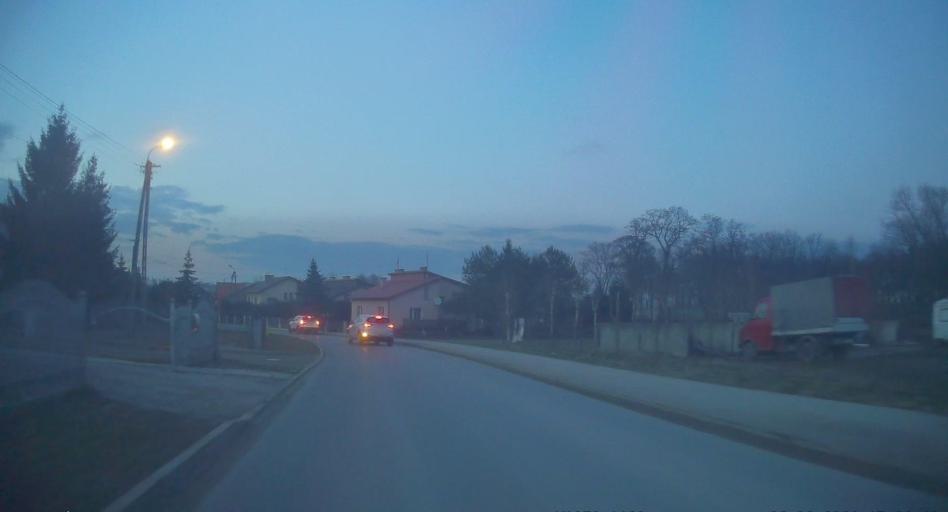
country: PL
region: Subcarpathian Voivodeship
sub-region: Powiat debicki
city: Debica
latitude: 50.0307
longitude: 21.3946
